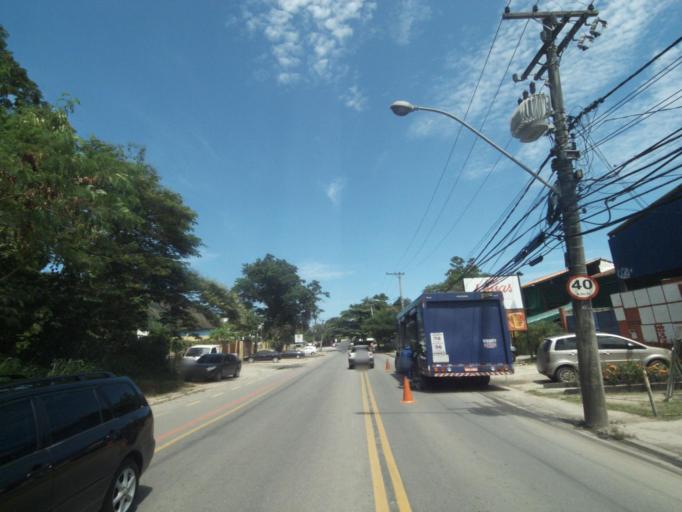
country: BR
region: Rio de Janeiro
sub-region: Niteroi
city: Niteroi
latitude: -22.9488
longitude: -43.0242
